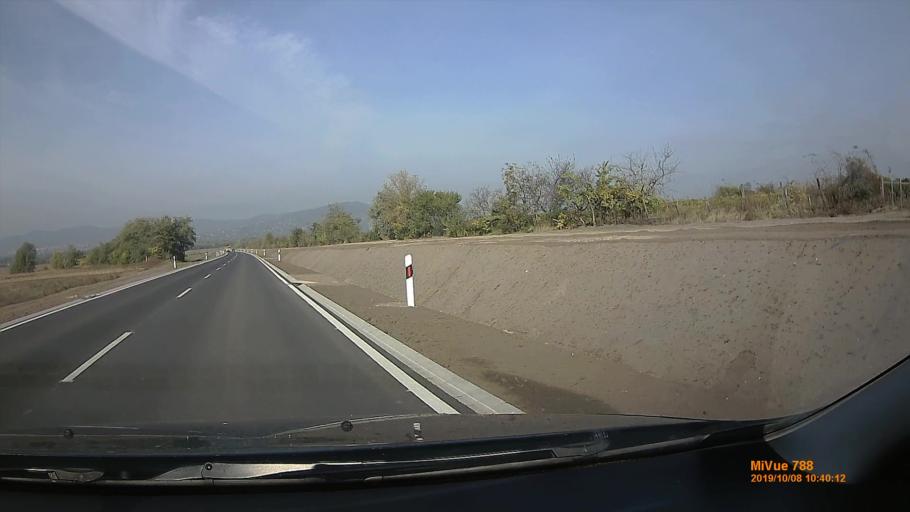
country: HU
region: Pest
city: Dunakeszi
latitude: 47.6601
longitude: 19.1492
